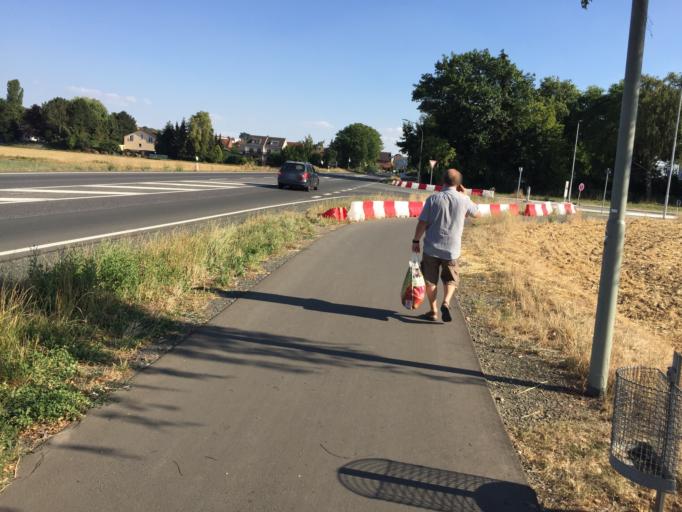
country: DE
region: Hesse
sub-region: Regierungsbezirk Giessen
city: Langgons
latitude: 50.5324
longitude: 8.6760
